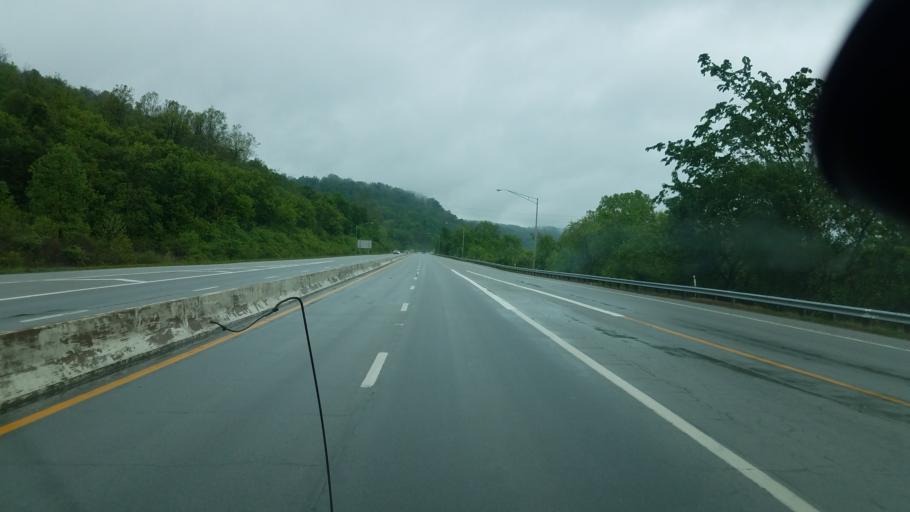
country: US
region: Ohio
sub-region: Belmont County
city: Yorkville
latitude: 40.1420
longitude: -80.7131
